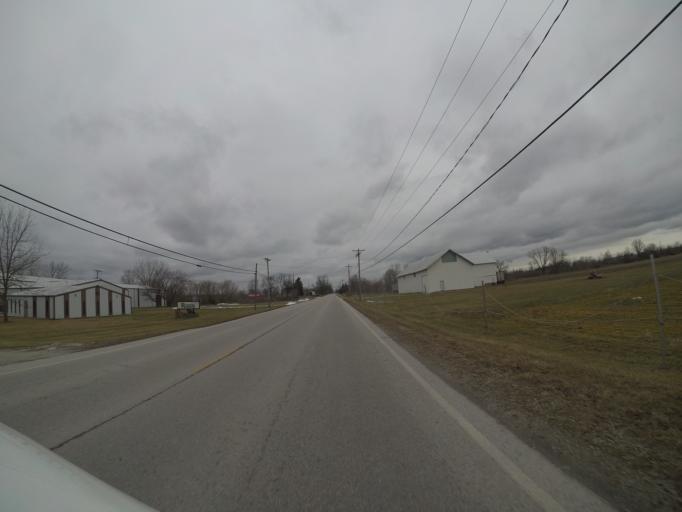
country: US
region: Ohio
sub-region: Wood County
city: Walbridge
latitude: 41.5683
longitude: -83.5120
